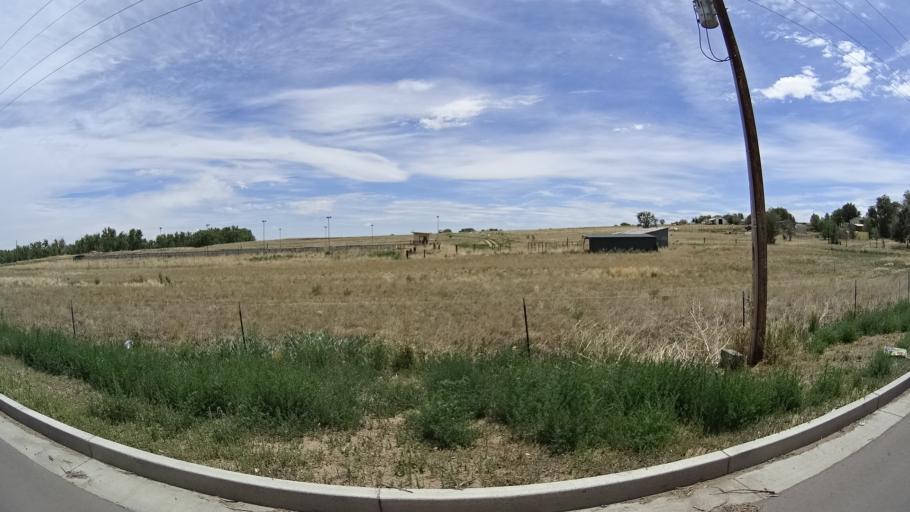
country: US
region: Colorado
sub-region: El Paso County
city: Fountain
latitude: 38.6980
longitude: -104.6736
